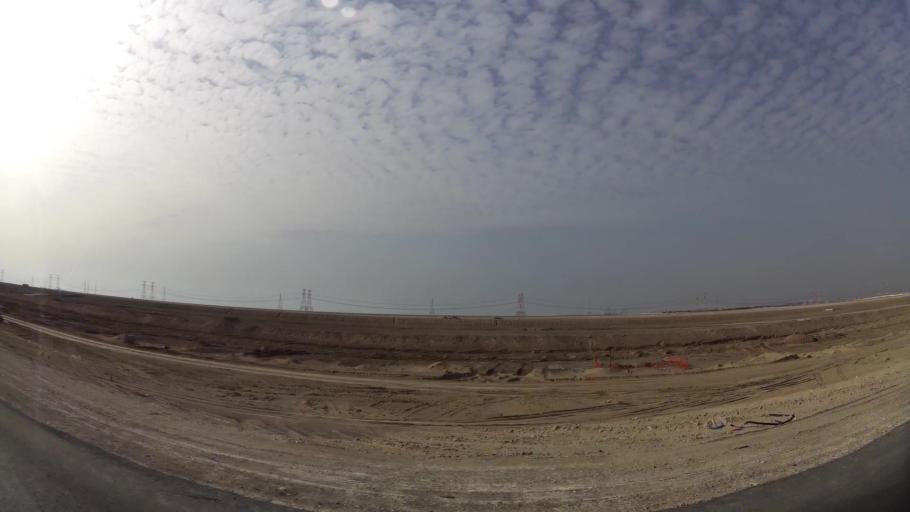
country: AE
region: Abu Dhabi
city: Abu Dhabi
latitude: 24.2340
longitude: 54.4589
